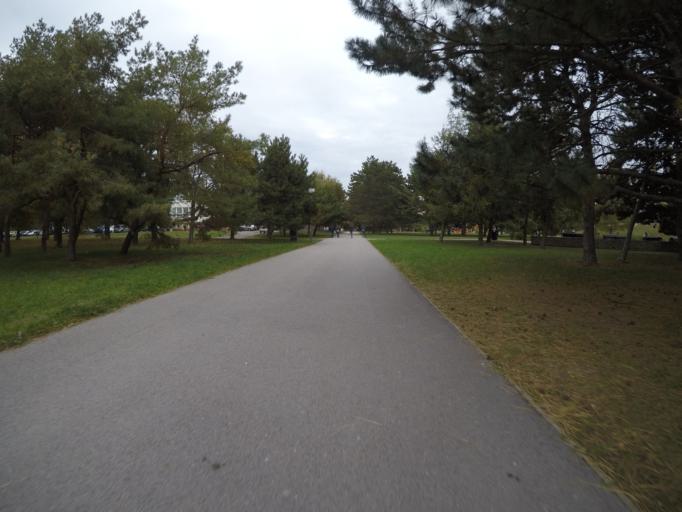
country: SK
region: Bratislavsky
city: Bratislava
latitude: 48.1617
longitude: 17.1676
